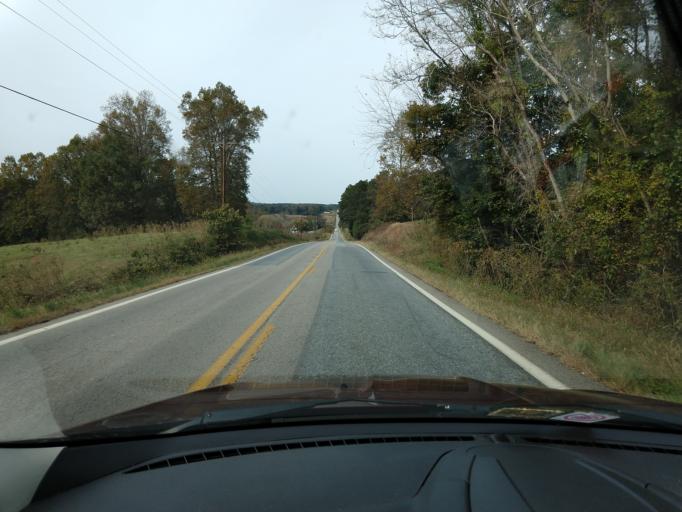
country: US
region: Virginia
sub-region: Pittsylvania County
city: Gretna
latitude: 36.9485
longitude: -79.5171
